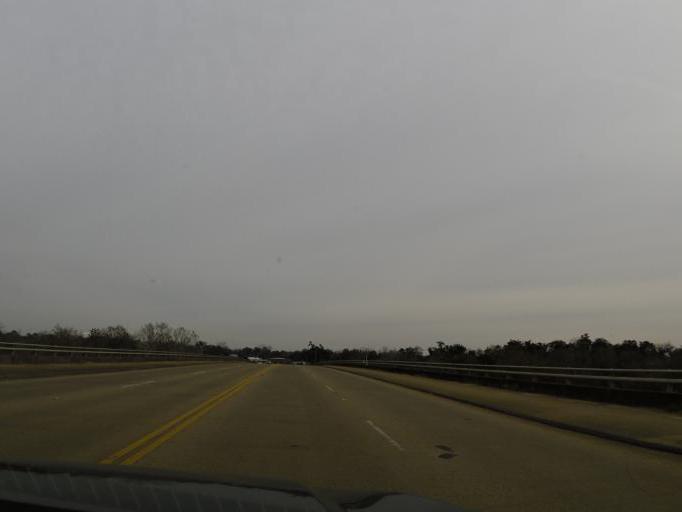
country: US
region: Georgia
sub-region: Decatur County
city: Bainbridge
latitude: 30.9107
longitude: -84.5815
